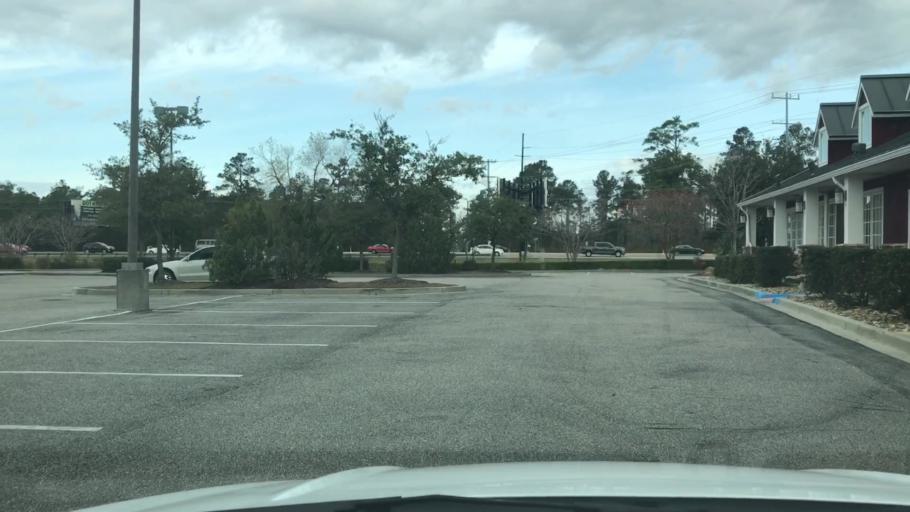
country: US
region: South Carolina
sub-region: Horry County
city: Myrtle Beach
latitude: 33.7058
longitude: -78.9206
